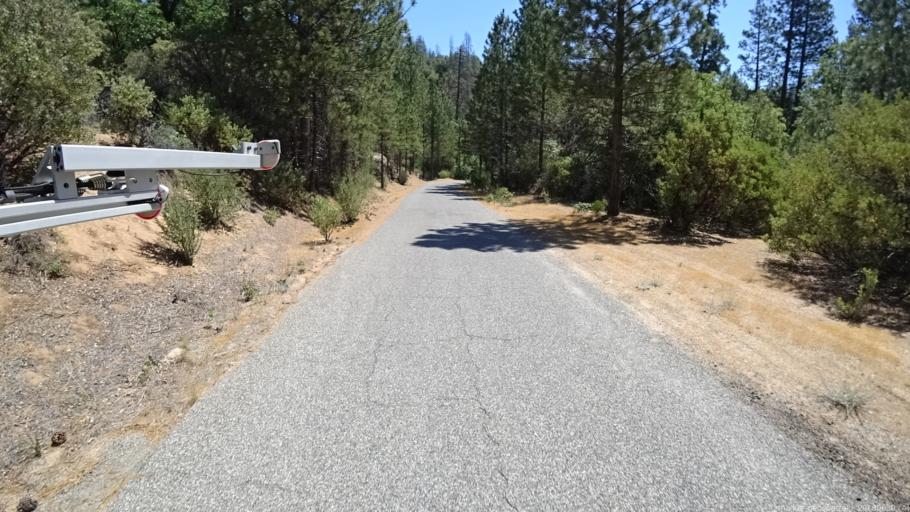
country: US
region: California
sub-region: Madera County
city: Oakhurst
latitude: 37.3591
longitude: -119.3457
